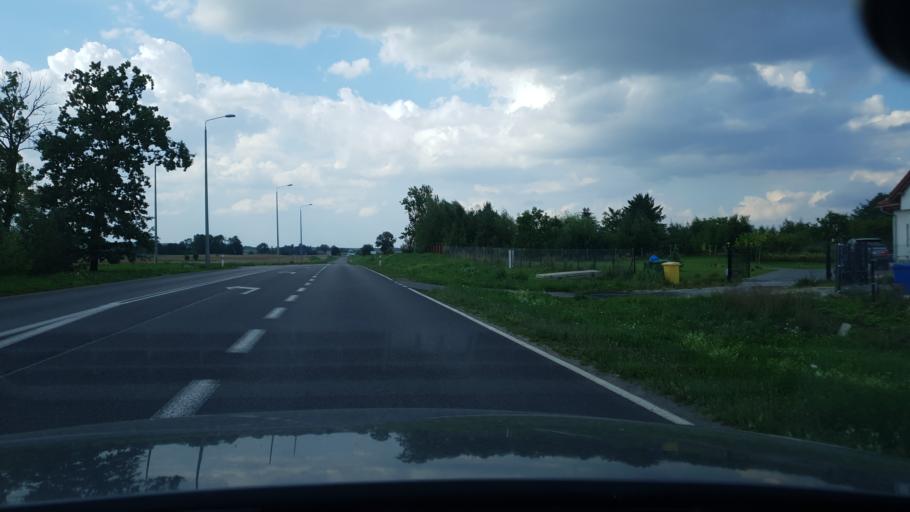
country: PL
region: Kujawsko-Pomorskie
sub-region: Powiat wabrzeski
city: Wabrzezno
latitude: 53.2864
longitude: 18.9280
